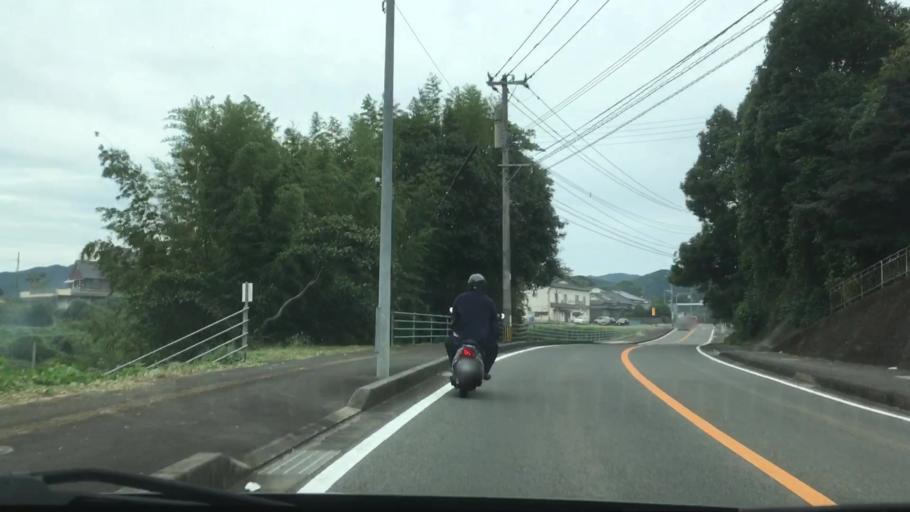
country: JP
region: Nagasaki
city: Sasebo
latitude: 33.0063
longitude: 129.7312
